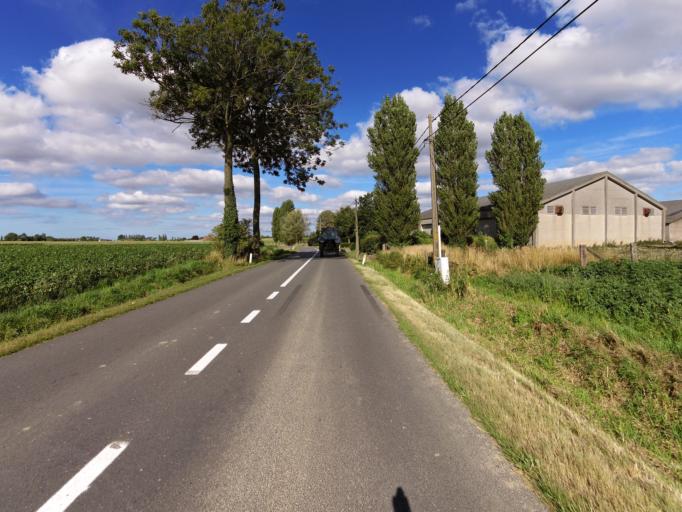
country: BE
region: Flanders
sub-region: Provincie West-Vlaanderen
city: Alveringem
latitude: 50.9628
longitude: 2.6604
